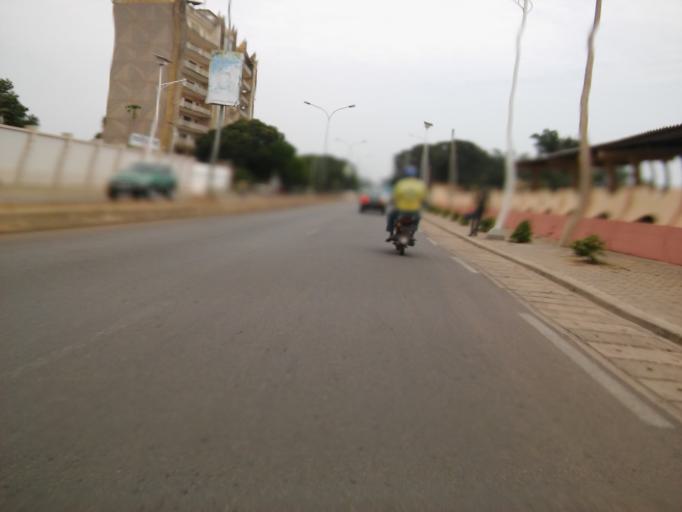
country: BJ
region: Littoral
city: Cotonou
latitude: 6.3534
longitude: 2.4020
